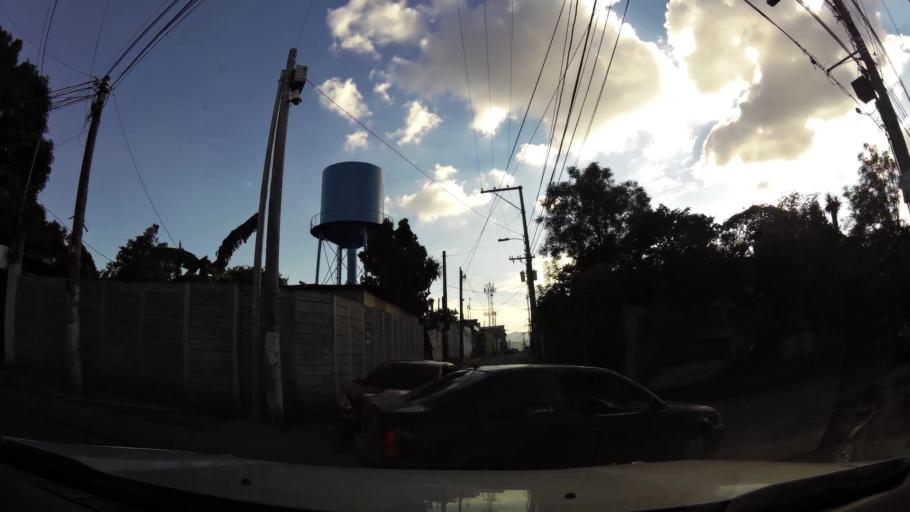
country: GT
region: Guatemala
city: Villa Nueva
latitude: 14.5259
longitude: -90.5815
